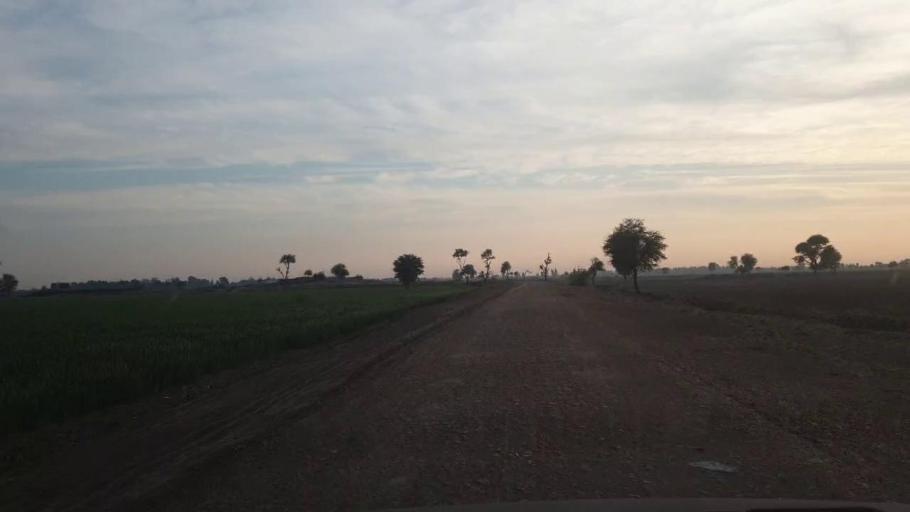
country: PK
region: Sindh
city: Shahpur Chakar
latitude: 26.0585
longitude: 68.5304
